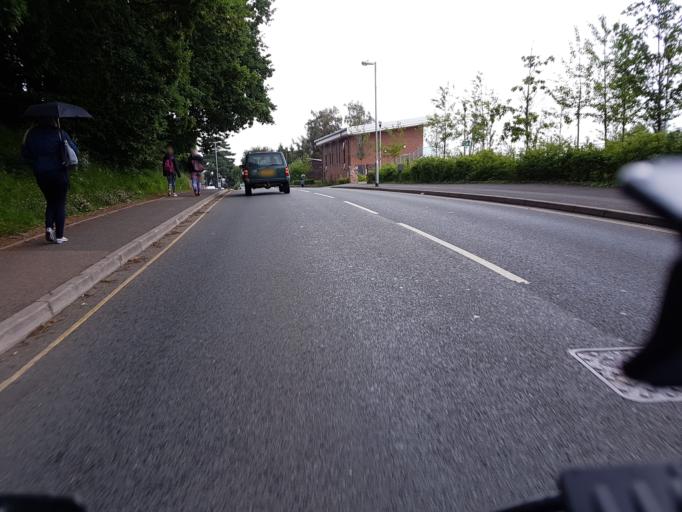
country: GB
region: England
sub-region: Devon
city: Exeter
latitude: 50.7342
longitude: -3.5296
